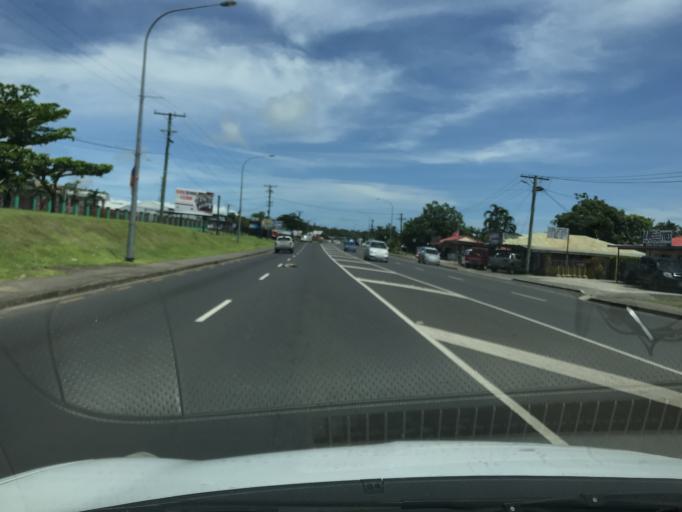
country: WS
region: Tuamasaga
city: Vaiusu
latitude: -13.8219
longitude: -171.8013
